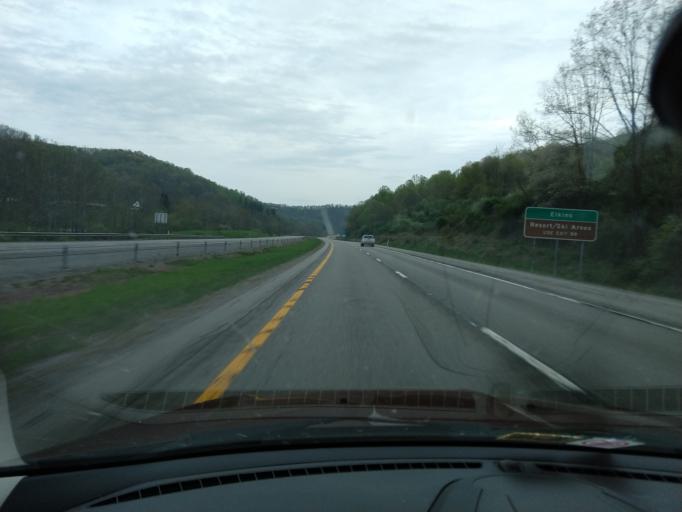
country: US
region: West Virginia
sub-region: Lewis County
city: Weston
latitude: 39.0001
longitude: -80.5012
